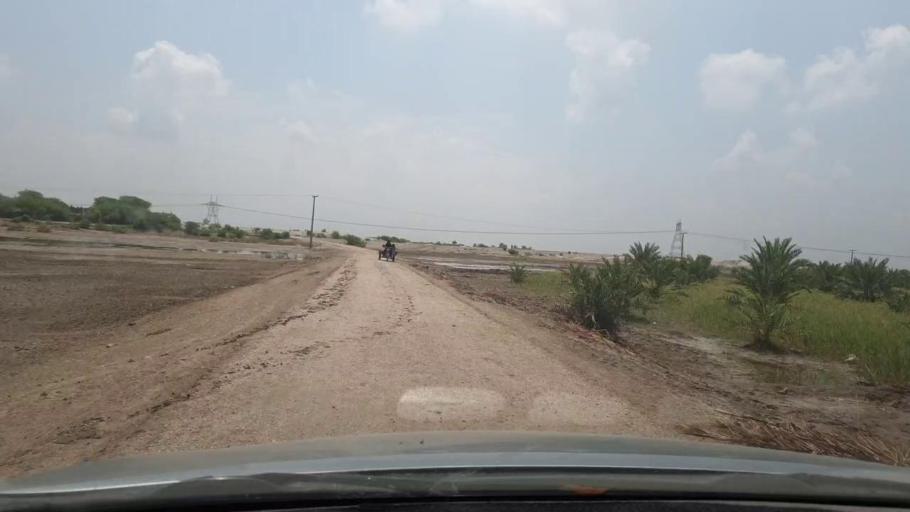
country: PK
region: Sindh
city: Khairpur
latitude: 27.4546
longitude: 68.7208
